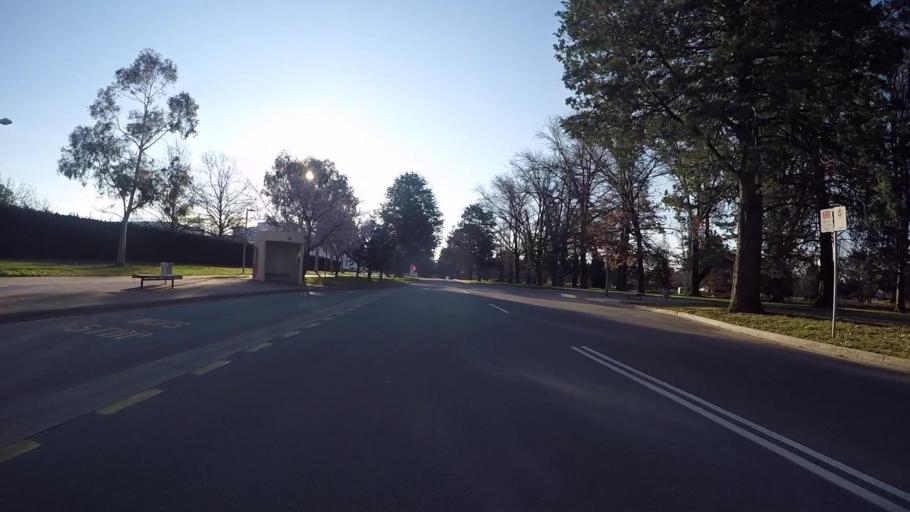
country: AU
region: Australian Capital Territory
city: Forrest
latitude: -35.3027
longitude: 149.1320
